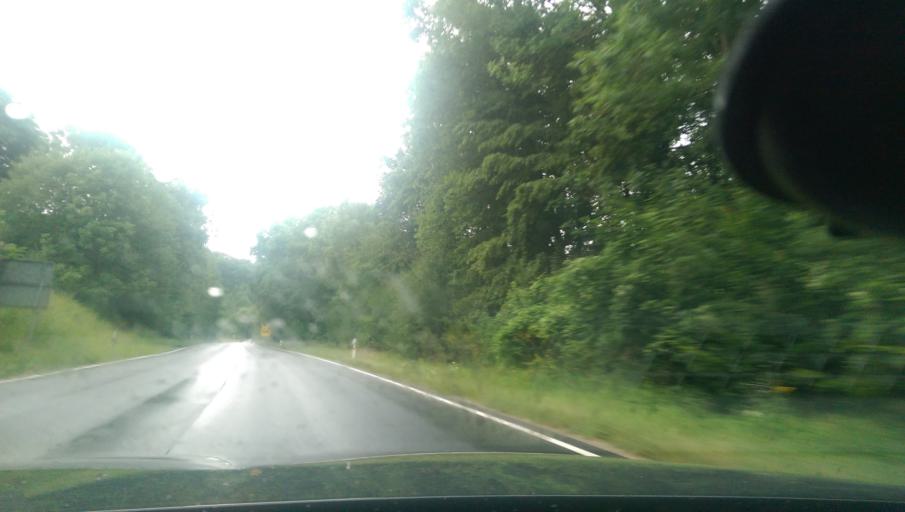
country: DE
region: Hesse
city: Witzenhausen
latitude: 51.3123
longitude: 9.8517
